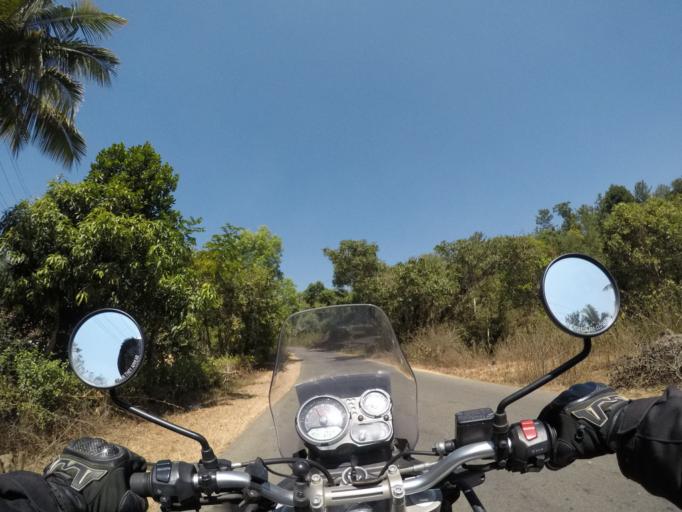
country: IN
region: Karnataka
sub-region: Chikmagalur
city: Mudigere
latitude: 13.0740
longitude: 75.6833
